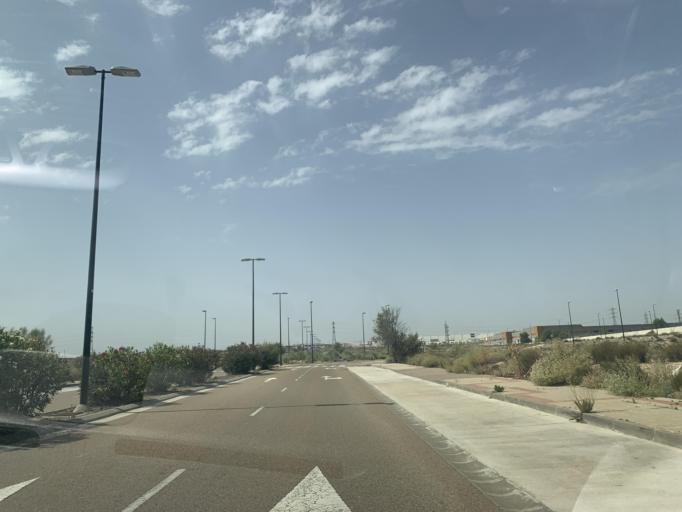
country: ES
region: Aragon
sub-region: Provincia de Zaragoza
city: Puebla de Alfinden
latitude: 41.5909
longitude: -0.8136
